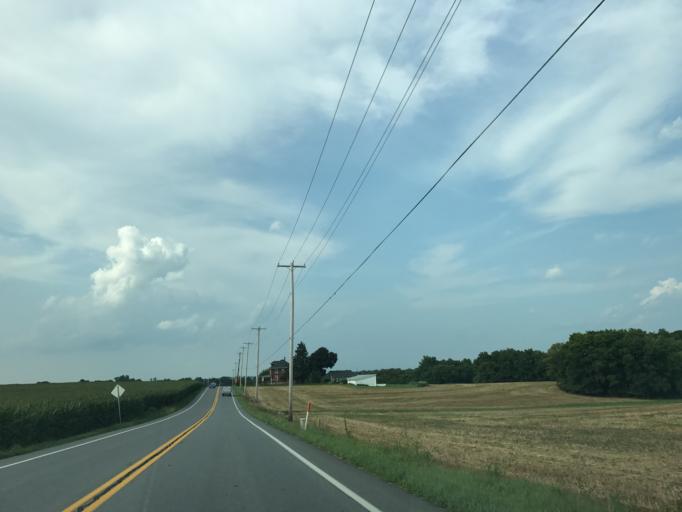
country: US
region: Pennsylvania
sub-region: Lancaster County
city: Marietta
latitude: 40.0746
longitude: -76.5387
